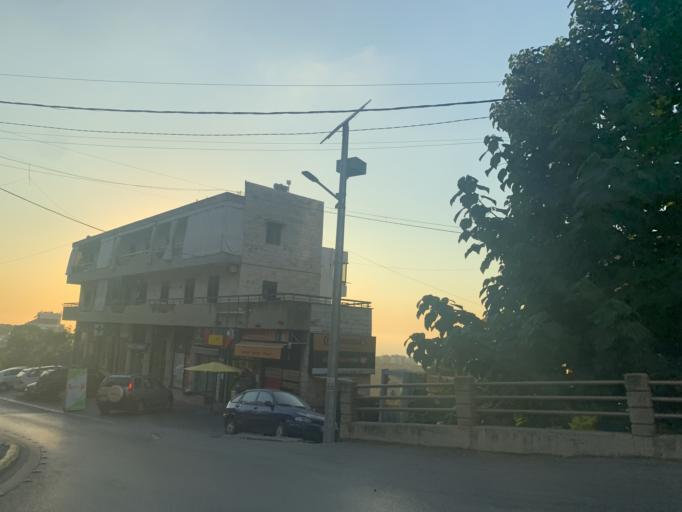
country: LB
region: Mont-Liban
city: Djounie
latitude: 33.9565
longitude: 35.6453
